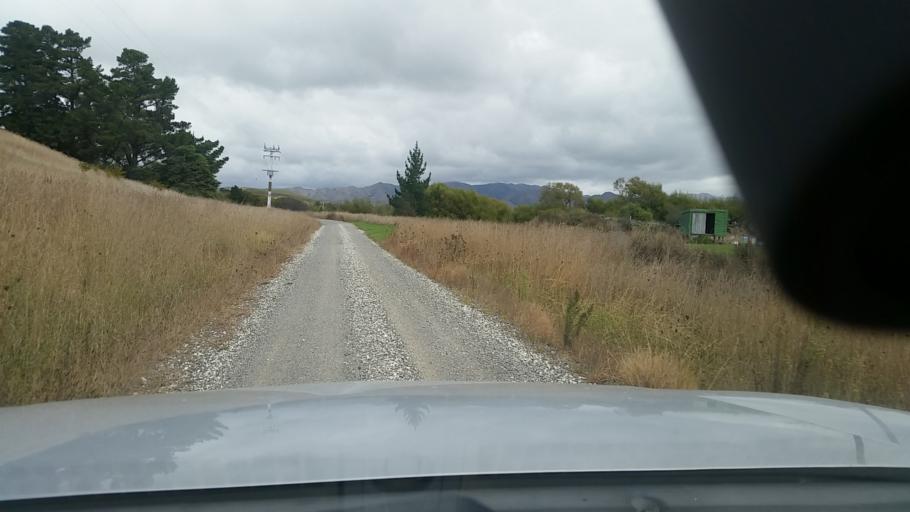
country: NZ
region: Marlborough
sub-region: Marlborough District
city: Blenheim
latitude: -41.6887
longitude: 174.1263
